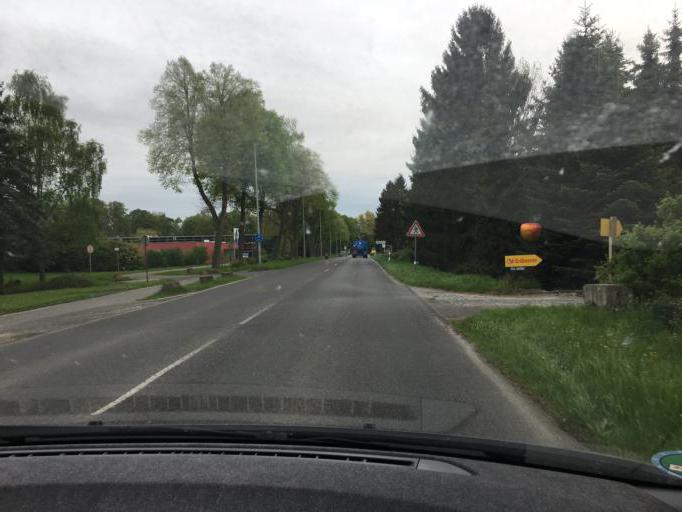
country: DE
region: North Rhine-Westphalia
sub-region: Regierungsbezirk Dusseldorf
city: Monchengladbach
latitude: 51.1203
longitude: 6.4130
